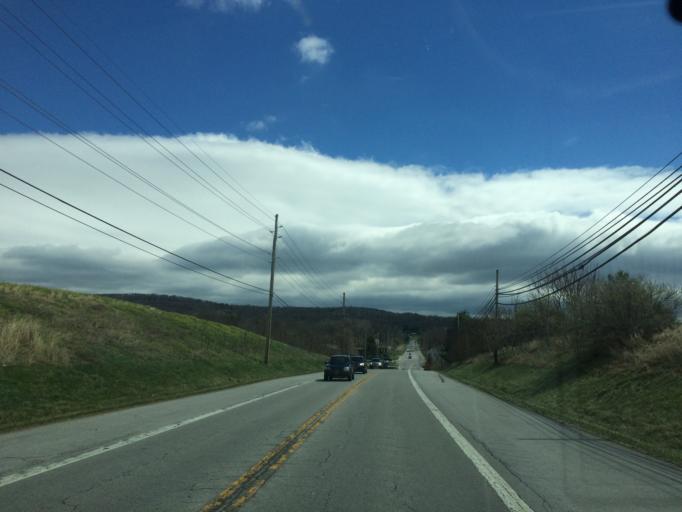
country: US
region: Maryland
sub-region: Frederick County
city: Middletown
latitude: 39.4360
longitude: -77.5227
